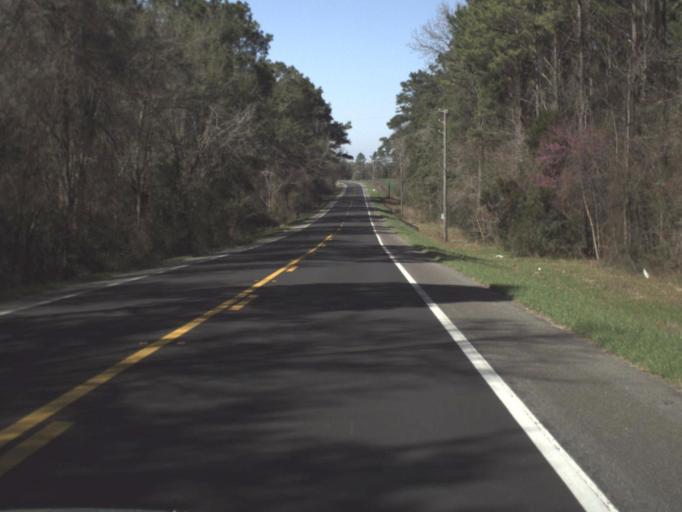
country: US
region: Florida
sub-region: Jackson County
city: Marianna
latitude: 30.6121
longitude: -85.1482
